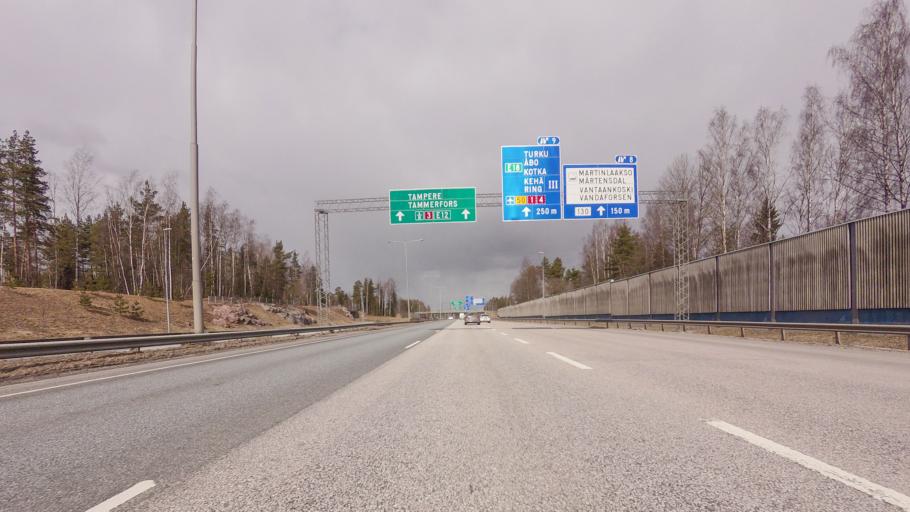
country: FI
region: Uusimaa
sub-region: Helsinki
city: Teekkarikylae
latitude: 60.2850
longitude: 24.8645
